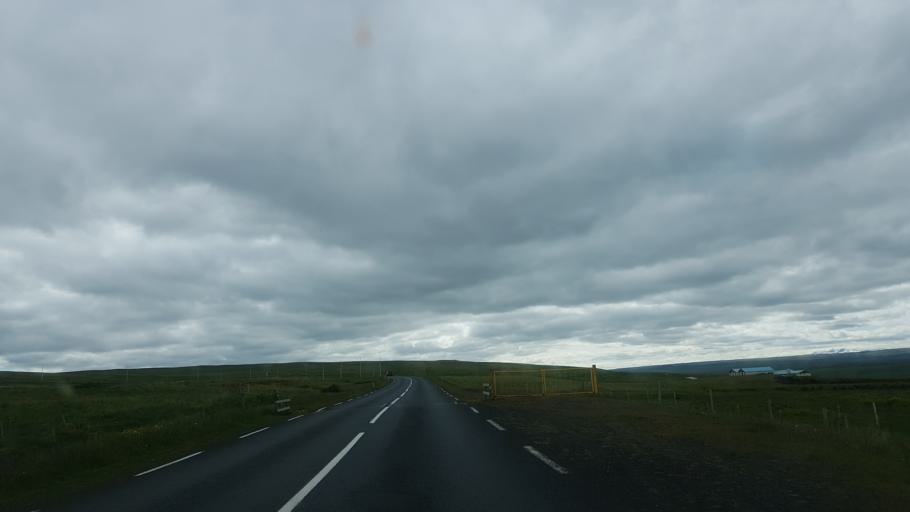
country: IS
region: Northwest
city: Saudarkrokur
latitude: 65.3565
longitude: -20.8888
